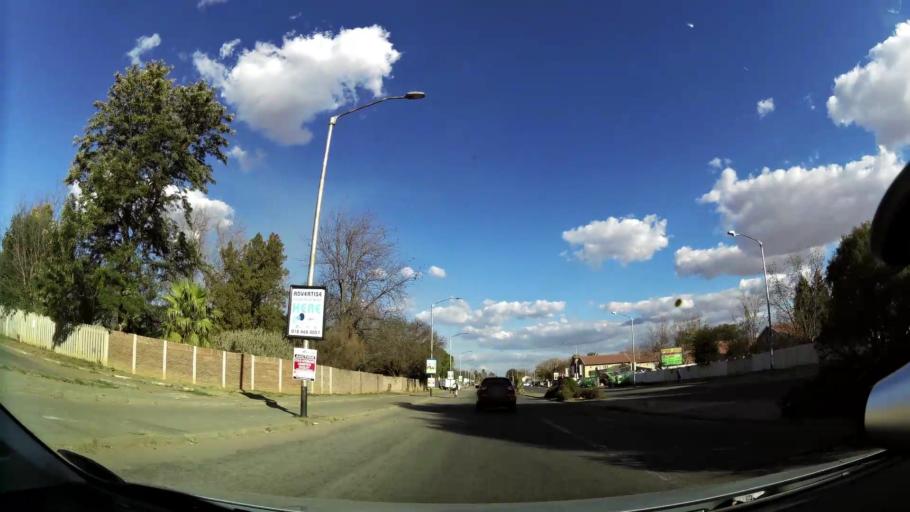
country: ZA
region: North-West
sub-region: Dr Kenneth Kaunda District Municipality
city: Klerksdorp
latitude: -26.8521
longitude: 26.6643
